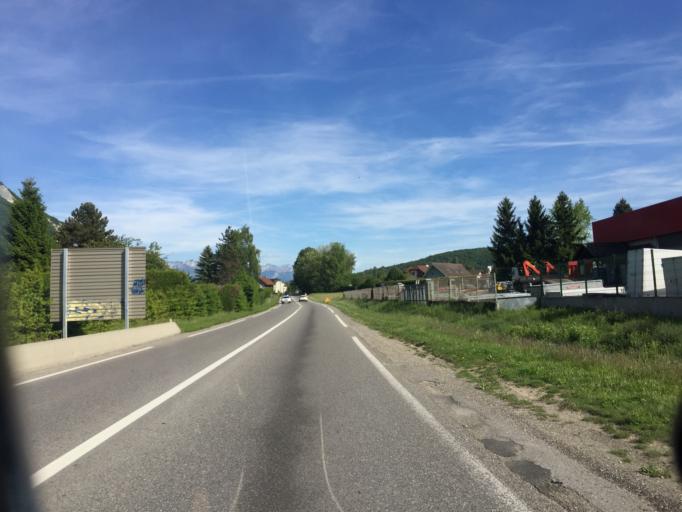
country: FR
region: Rhone-Alpes
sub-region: Departement de la Haute-Savoie
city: La Balme-de-Sillingy
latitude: 45.9540
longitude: 6.0390
